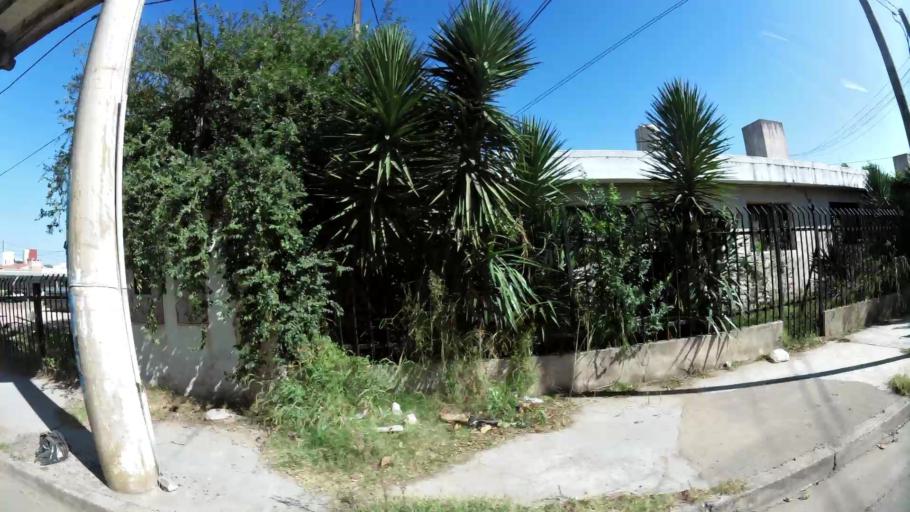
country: AR
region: Cordoba
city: Villa Allende
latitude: -31.3380
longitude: -64.2414
